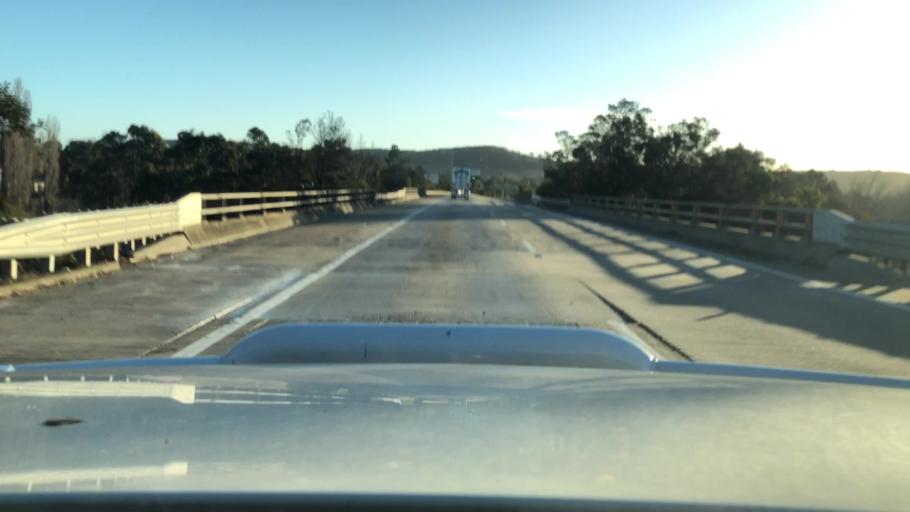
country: AU
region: New South Wales
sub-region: Goulburn Mulwaree
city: Goulburn
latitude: -34.7103
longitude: 150.0104
